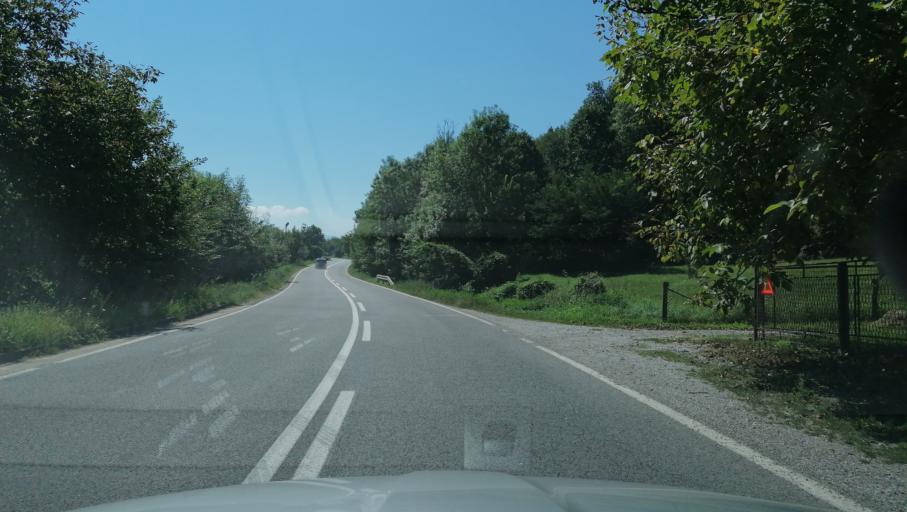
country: RS
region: Central Serbia
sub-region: Raski Okrug
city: Kraljevo
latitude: 43.7197
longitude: 20.7964
